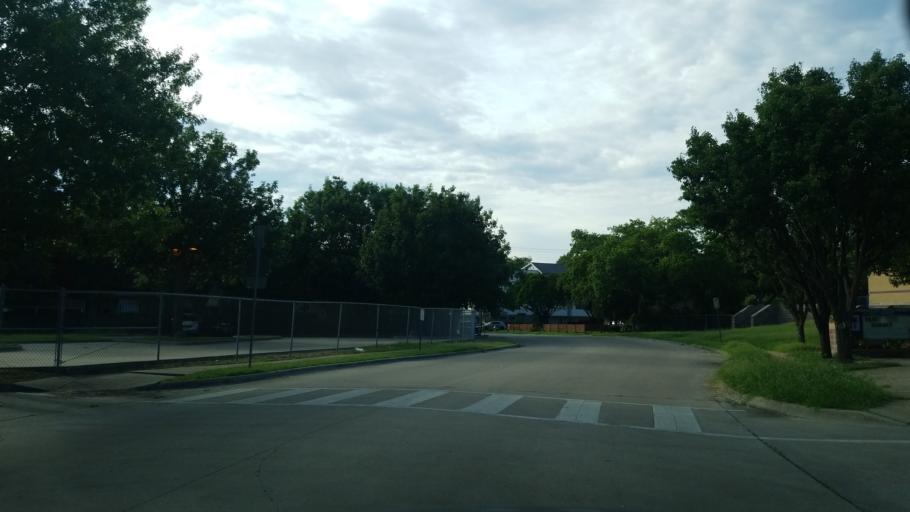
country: US
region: Texas
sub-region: Dallas County
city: Highland Park
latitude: 32.8098
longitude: -96.7751
